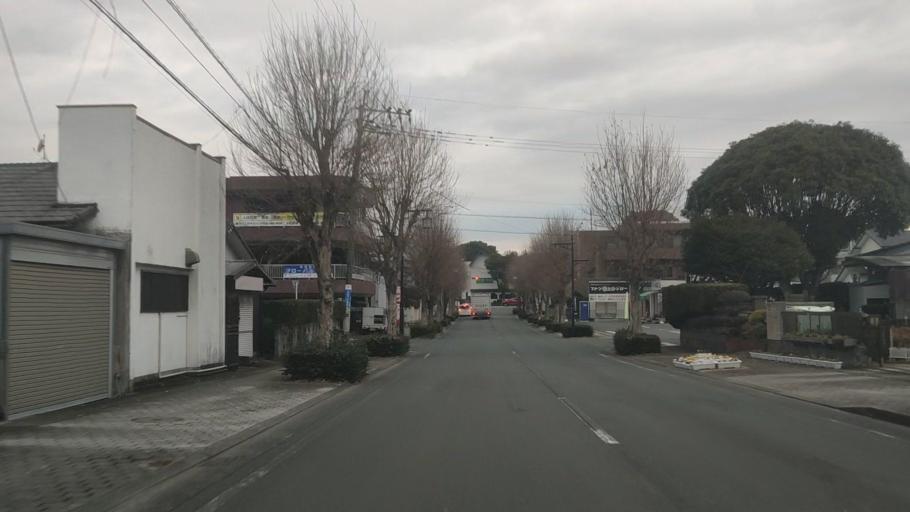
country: JP
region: Kumamoto
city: Kumamoto
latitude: 32.8158
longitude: 130.7533
